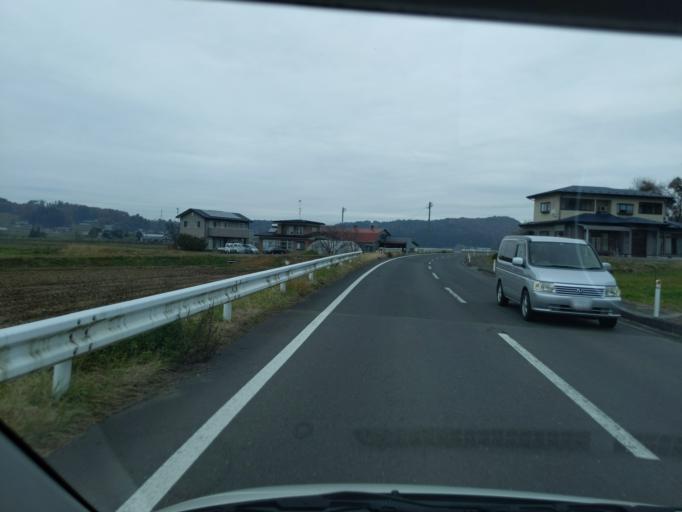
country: JP
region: Iwate
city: Mizusawa
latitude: 39.1707
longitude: 141.2128
